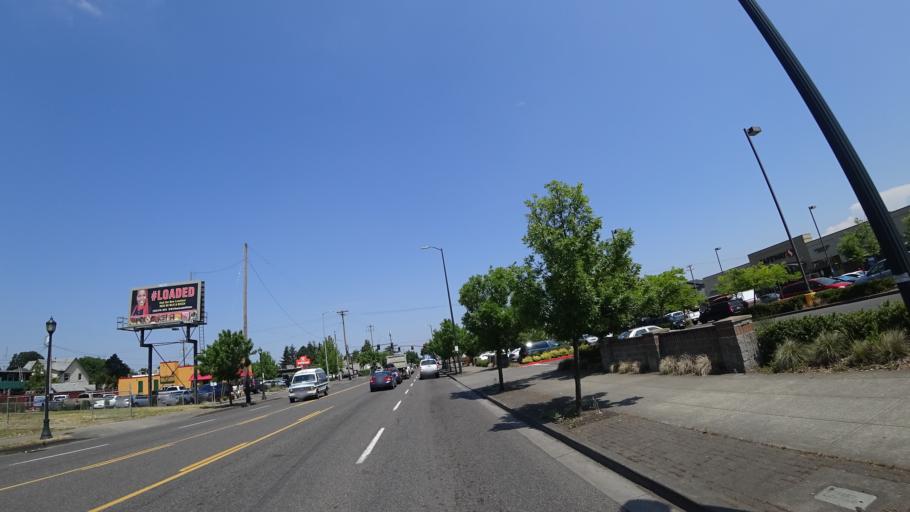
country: US
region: Oregon
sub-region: Multnomah County
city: Portland
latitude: 45.5656
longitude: -122.6614
